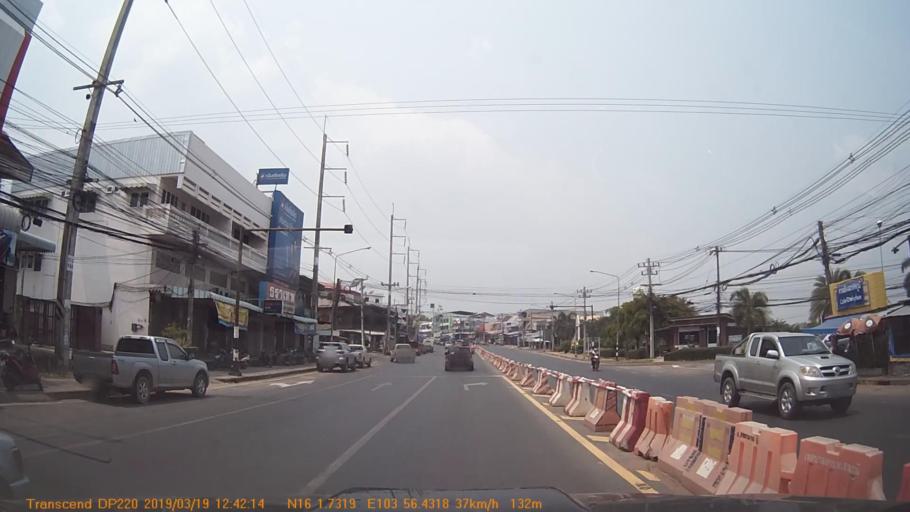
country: TH
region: Roi Et
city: Selaphum
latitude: 16.0290
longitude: 103.9404
